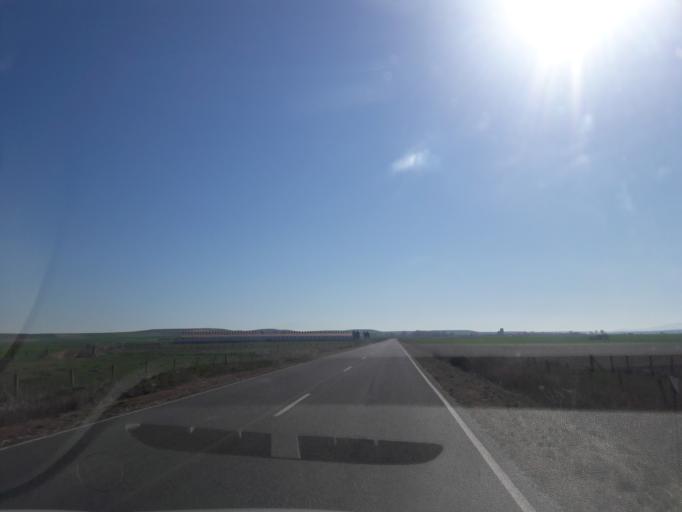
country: ES
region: Castille and Leon
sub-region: Provincia de Salamanca
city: Salmoral
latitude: 40.8098
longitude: -5.2456
